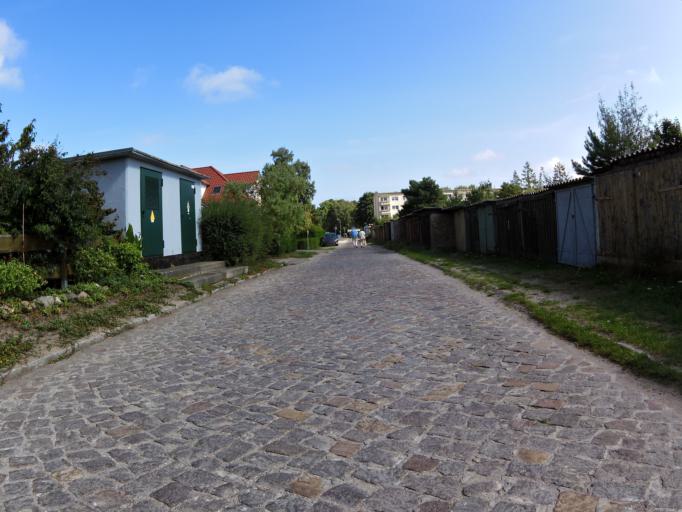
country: DE
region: Mecklenburg-Vorpommern
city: Karlshagen
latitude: 54.1199
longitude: 13.8295
